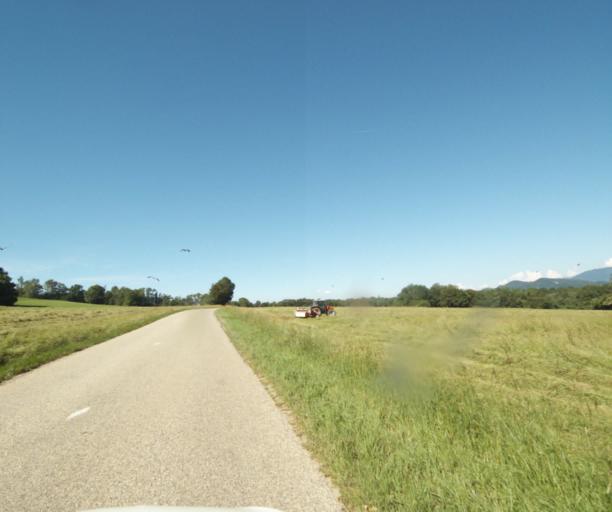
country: FR
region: Rhone-Alpes
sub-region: Departement de la Haute-Savoie
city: Sciez
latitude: 46.3023
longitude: 6.3786
